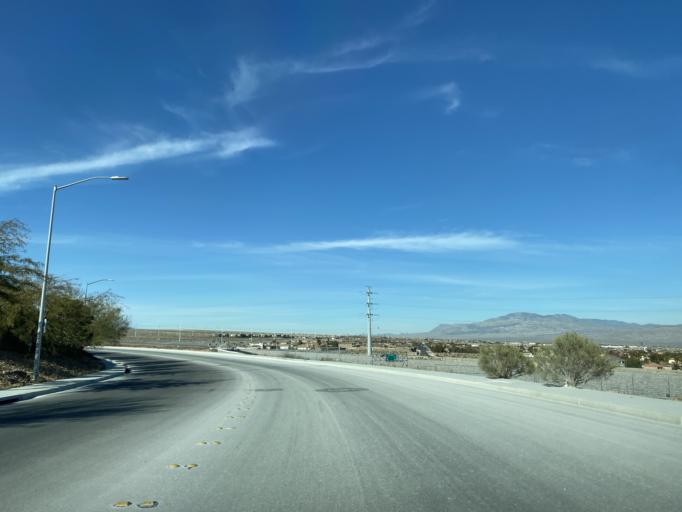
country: US
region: Nevada
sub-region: Clark County
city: Summerlin South
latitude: 36.2579
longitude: -115.3241
